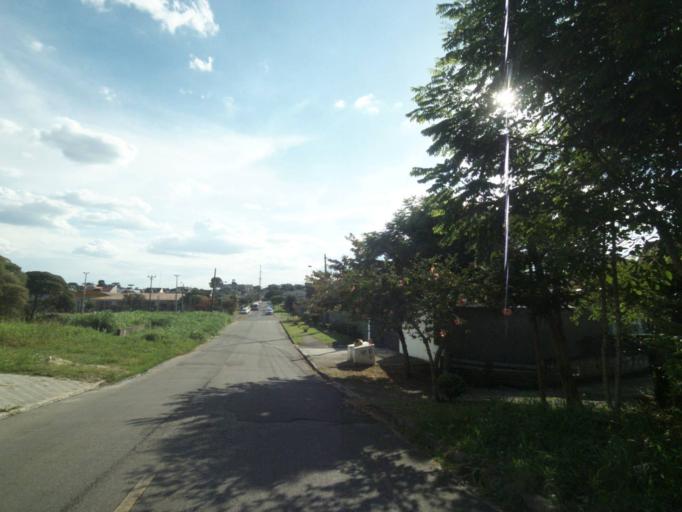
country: BR
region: Parana
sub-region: Pinhais
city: Pinhais
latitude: -25.4710
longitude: -49.2262
